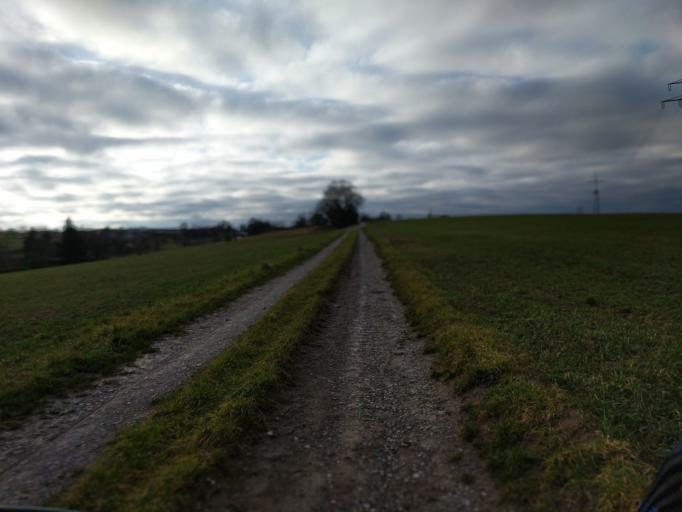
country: DE
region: Baden-Wuerttemberg
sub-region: Tuebingen Region
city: Rottenburg
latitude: 48.4963
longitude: 8.9474
